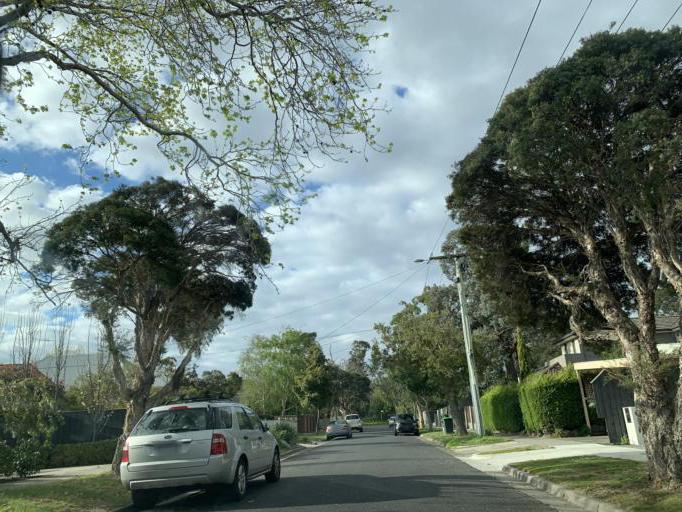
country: AU
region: Victoria
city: Beaumaris
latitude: -37.9836
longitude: 145.0394
